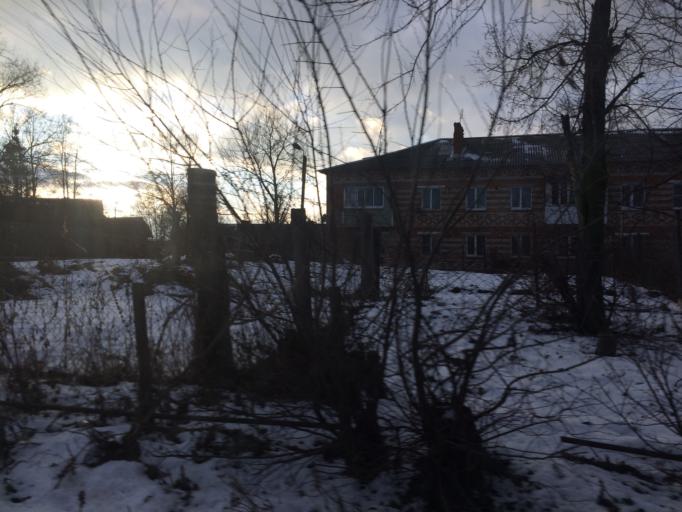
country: RU
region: Tula
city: Cherepet'
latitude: 54.1087
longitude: 36.3284
